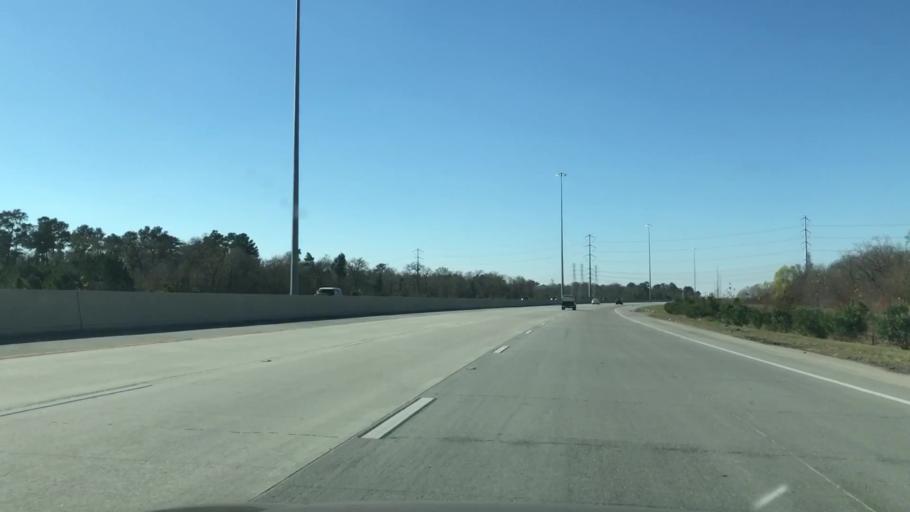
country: US
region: Texas
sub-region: Harris County
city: Jacinto City
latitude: 29.7970
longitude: -95.2262
